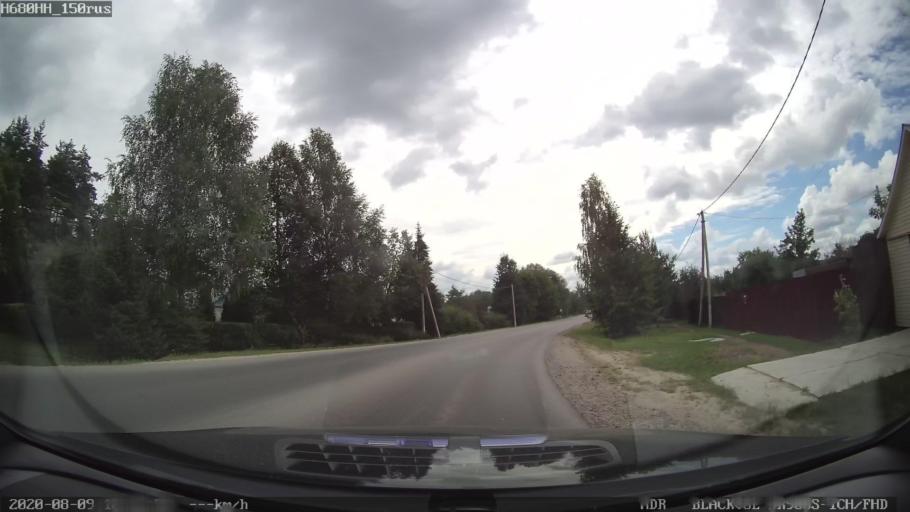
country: RU
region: Tula
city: Zaokskiy
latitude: 54.7424
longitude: 37.3921
